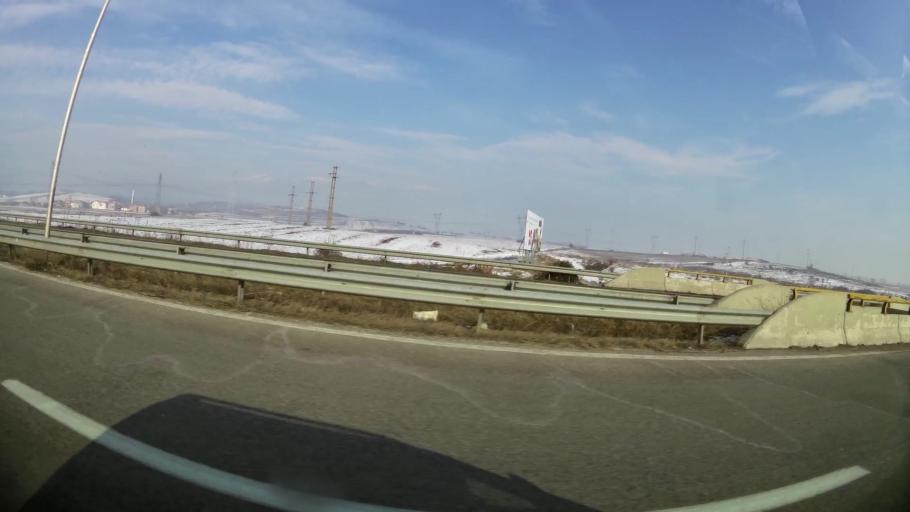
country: MK
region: Butel
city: Butel
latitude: 42.0368
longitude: 21.4672
